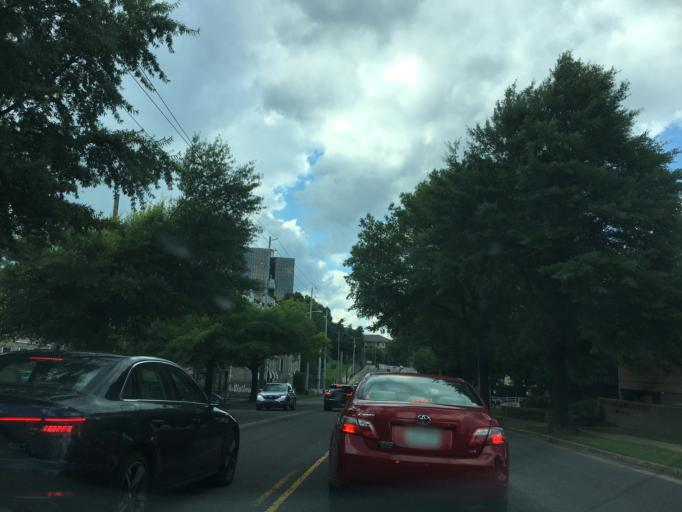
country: US
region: Tennessee
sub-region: Davidson County
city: Nashville
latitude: 36.1415
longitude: -86.8146
